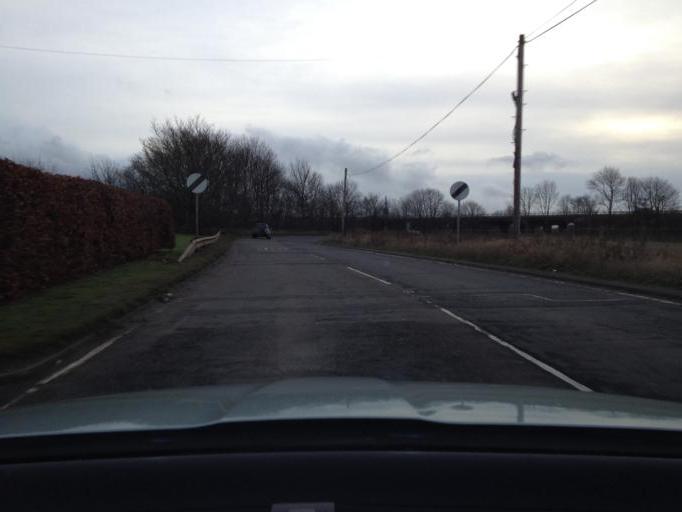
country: GB
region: Scotland
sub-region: Edinburgh
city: Kirkliston
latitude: 55.9489
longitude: -3.4066
